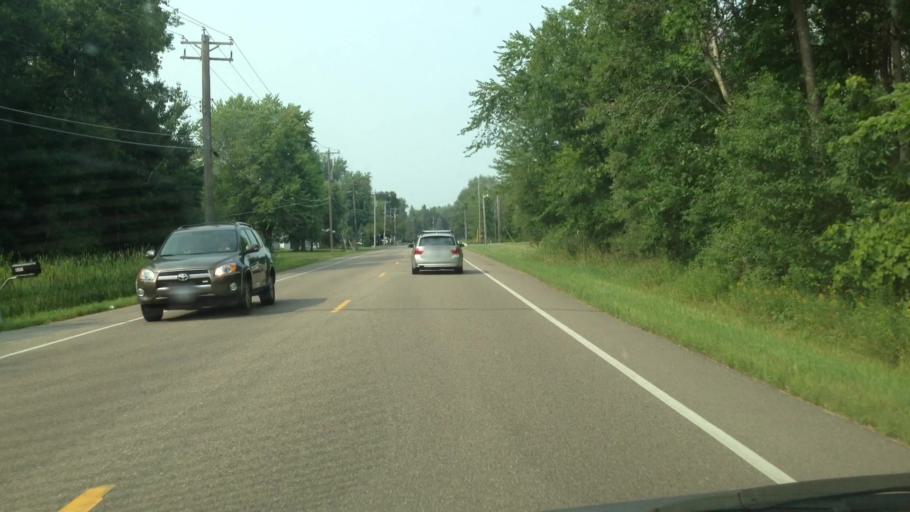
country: US
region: Minnesota
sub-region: Anoka County
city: Circle Pines
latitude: 45.1332
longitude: -93.1273
